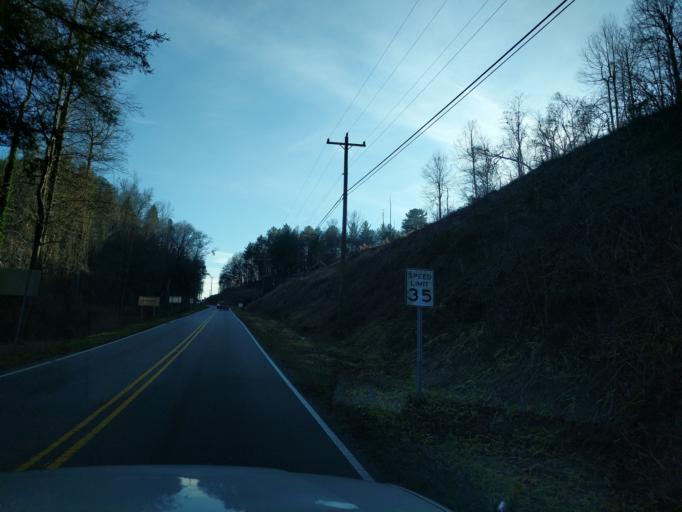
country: US
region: North Carolina
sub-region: Rutherford County
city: Lake Lure
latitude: 35.4151
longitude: -82.1962
